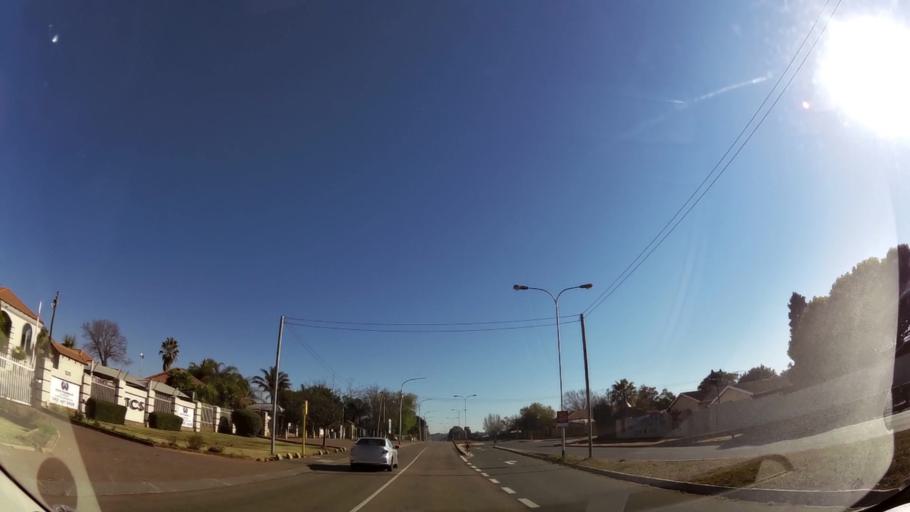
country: ZA
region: Gauteng
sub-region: City of Tshwane Metropolitan Municipality
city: Centurion
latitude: -25.8598
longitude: 28.2075
